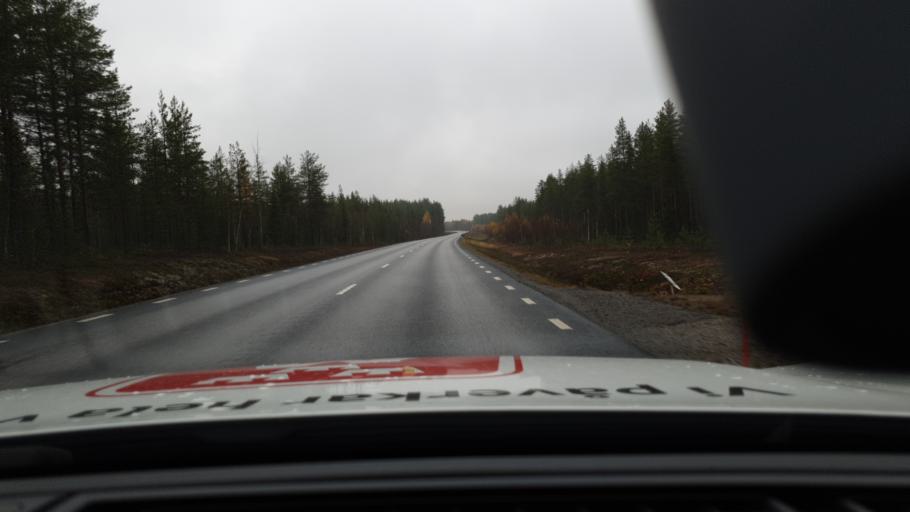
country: SE
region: Norrbotten
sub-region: Overkalix Kommun
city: OEverkalix
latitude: 66.6346
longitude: 22.2048
